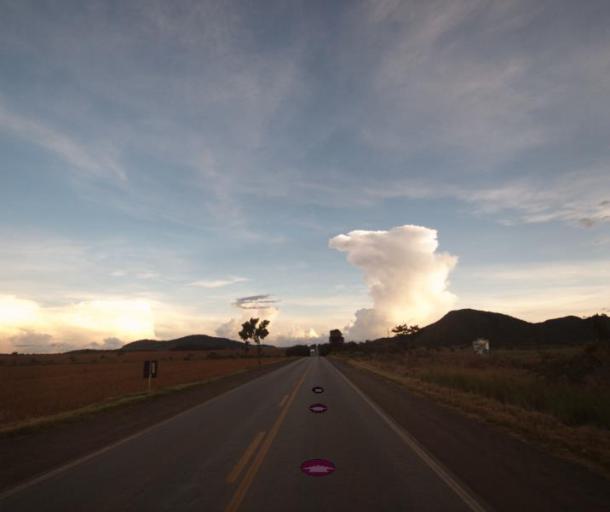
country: BR
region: Goias
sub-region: Uruacu
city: Uruacu
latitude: -14.3717
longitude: -49.1583
